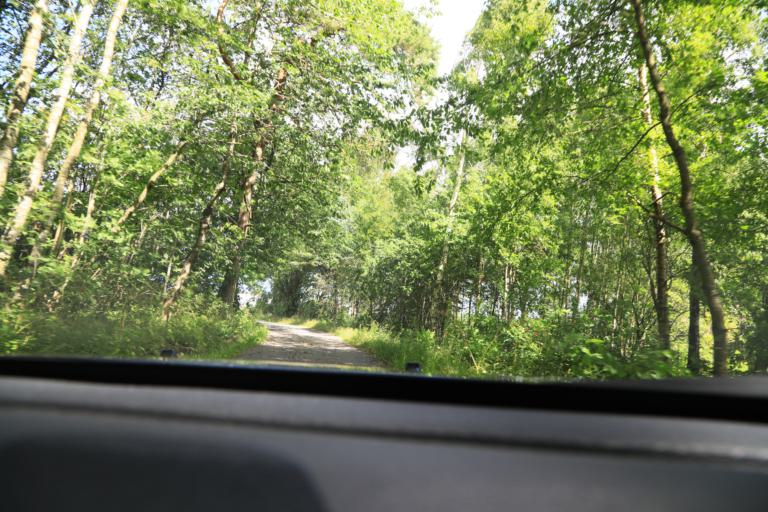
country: SE
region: Halland
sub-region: Varbergs Kommun
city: Traslovslage
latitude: 57.0948
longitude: 12.2940
